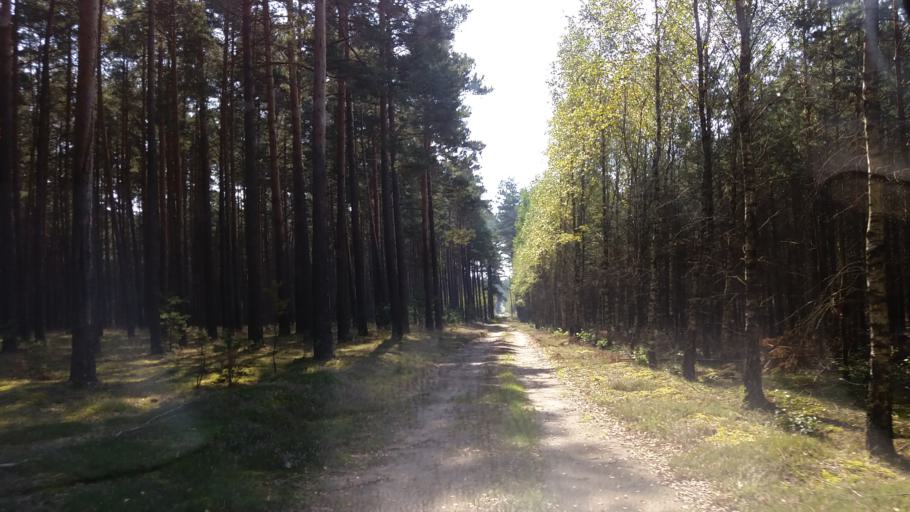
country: PL
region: West Pomeranian Voivodeship
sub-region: Powiat drawski
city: Kalisz Pomorski
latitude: 53.1956
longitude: 15.8959
